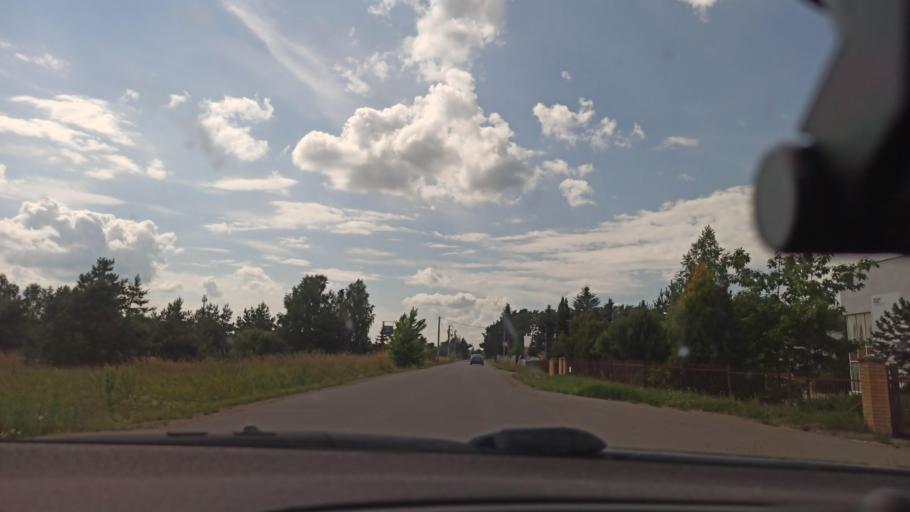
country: PL
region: Podlasie
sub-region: Powiat bialostocki
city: Turosn Koscielna
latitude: 53.0682
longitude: 23.0869
